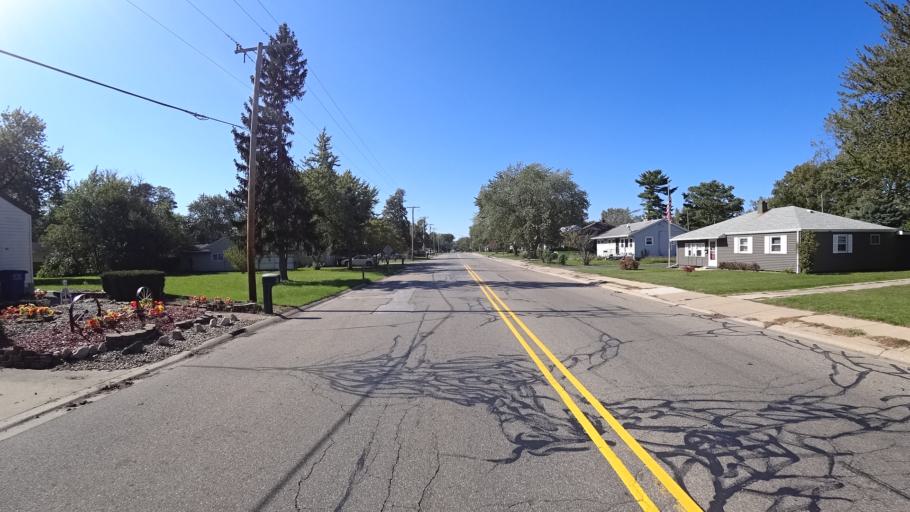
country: US
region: Indiana
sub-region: LaPorte County
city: Michigan City
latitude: 41.6948
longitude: -86.8959
